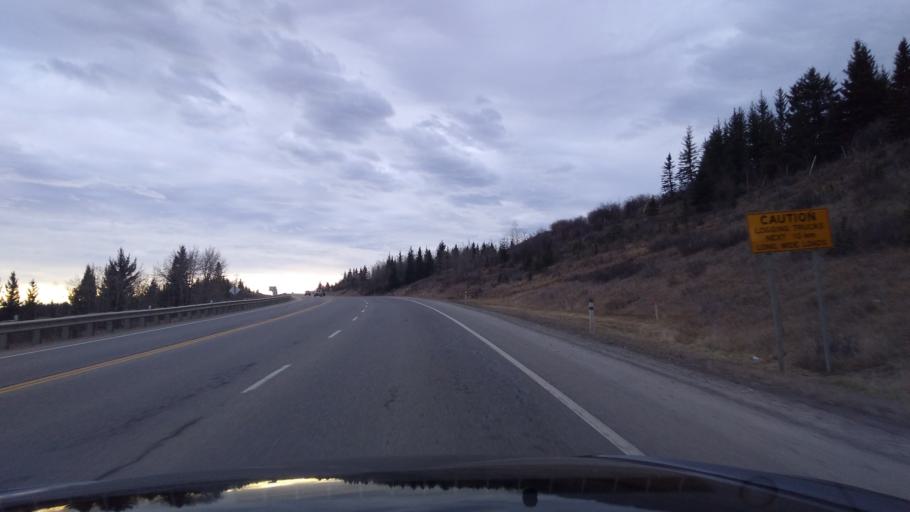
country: CA
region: Alberta
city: Cochrane
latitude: 51.1775
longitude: -114.4869
